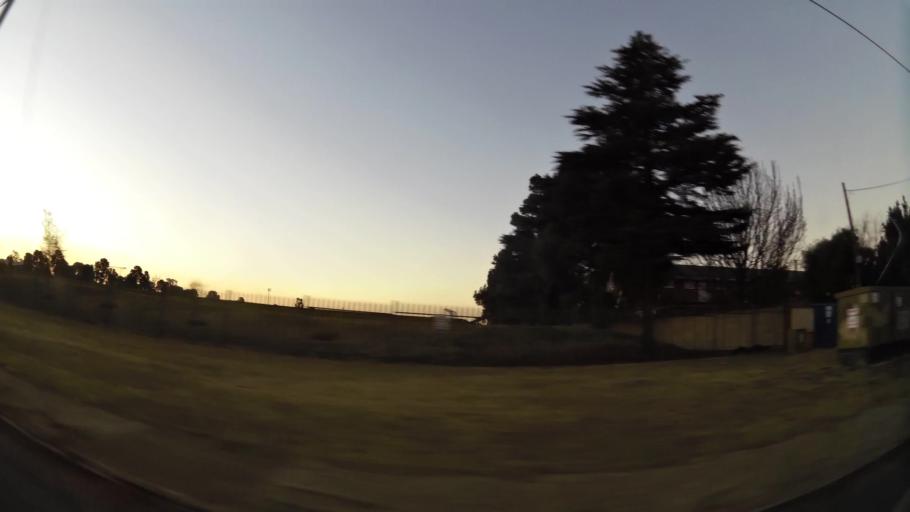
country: ZA
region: Gauteng
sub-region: City of Johannesburg Metropolitan Municipality
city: Roodepoort
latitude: -26.1708
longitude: 27.9216
